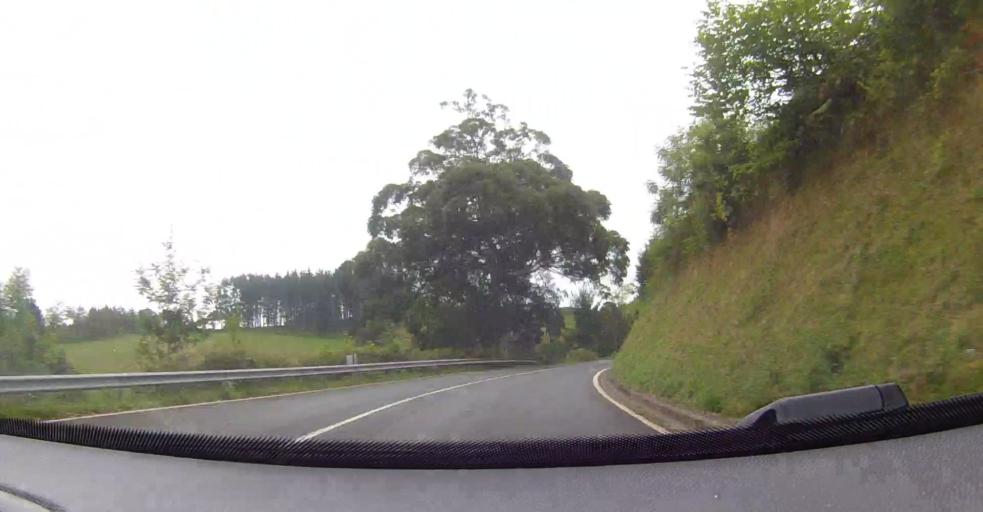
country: ES
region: Basque Country
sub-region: Bizkaia
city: Balmaseda
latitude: 43.2292
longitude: -3.1945
